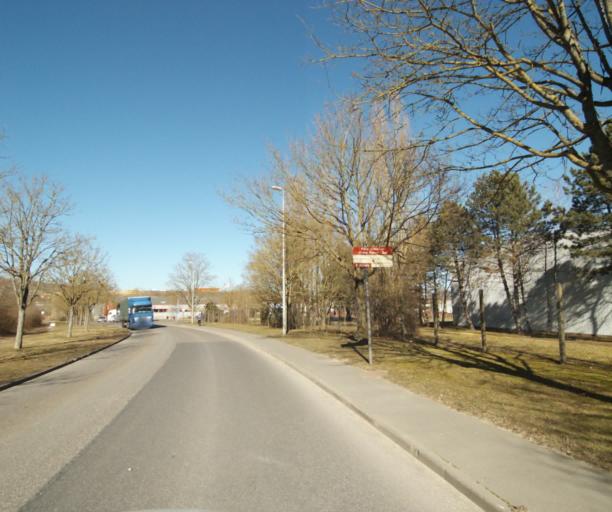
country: FR
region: Lorraine
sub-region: Departement de Meurthe-et-Moselle
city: Fleville-devant-Nancy
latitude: 48.6143
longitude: 6.1925
